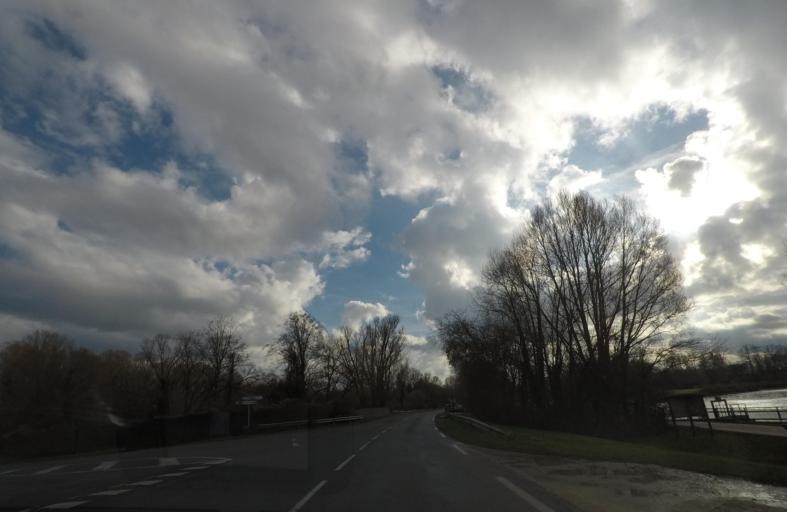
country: FR
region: Centre
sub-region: Departement du Cher
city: Bourges
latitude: 47.0495
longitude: 2.4084
